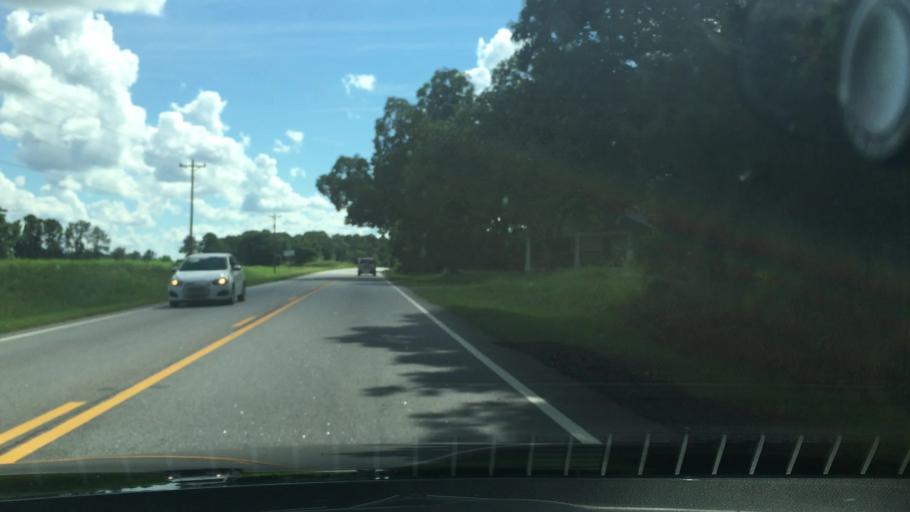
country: US
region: Georgia
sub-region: Butts County
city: Jackson
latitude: 33.2812
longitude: -84.0435
